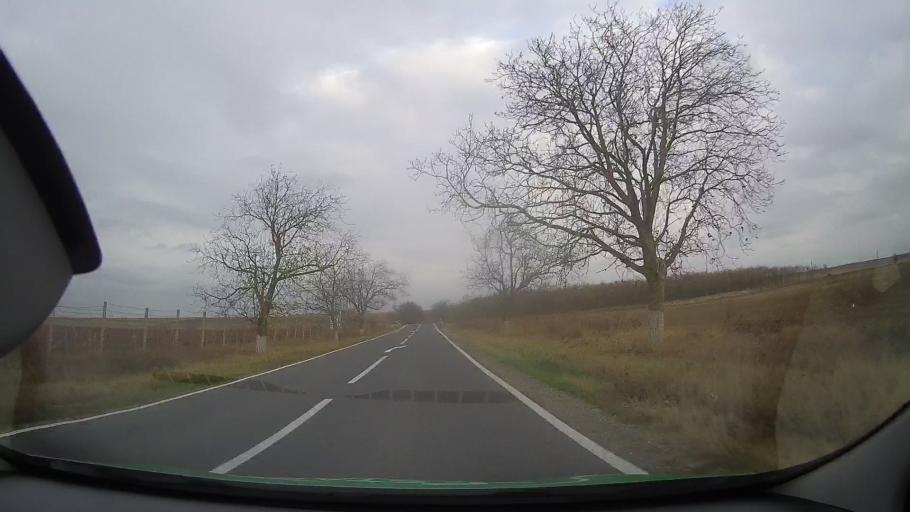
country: RO
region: Constanta
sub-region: Comuna Adamclisi
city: Adamclisi
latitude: 44.0880
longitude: 27.9716
